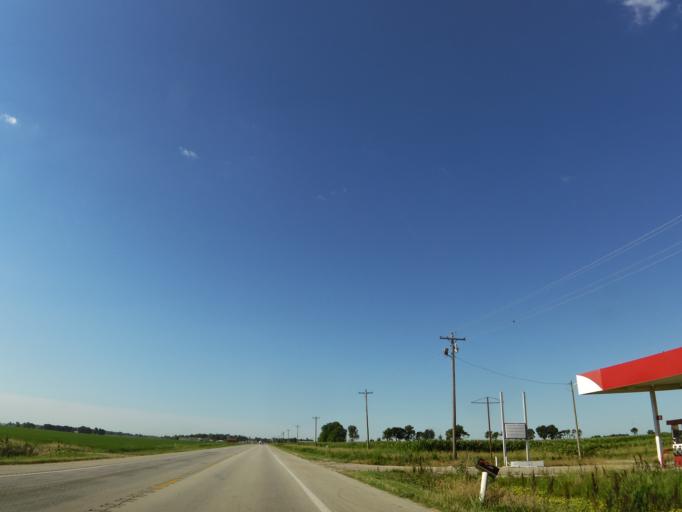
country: US
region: Arkansas
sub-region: Clay County
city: Corning
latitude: 36.5107
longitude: -90.5397
